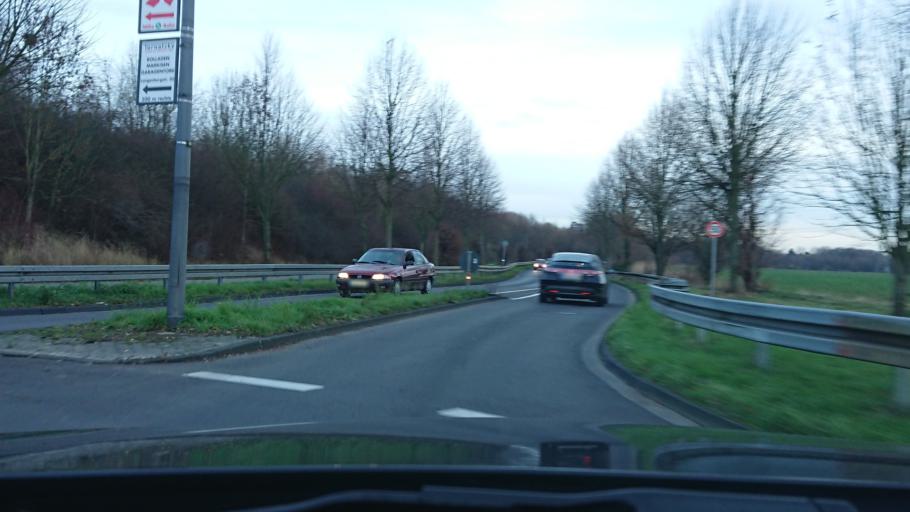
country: DE
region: North Rhine-Westphalia
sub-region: Regierungsbezirk Koln
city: Mengenich
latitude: 51.0338
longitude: 6.8818
